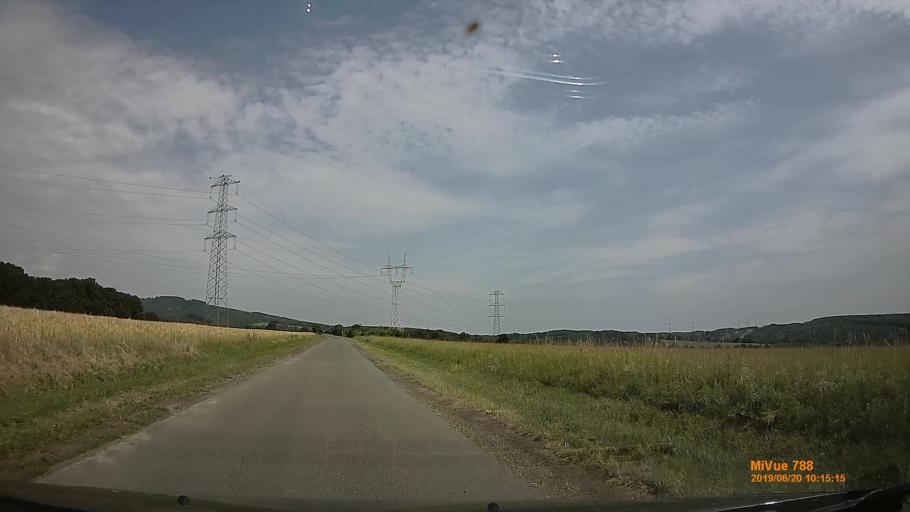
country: HU
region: Baranya
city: Mecseknadasd
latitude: 46.1902
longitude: 18.4657
